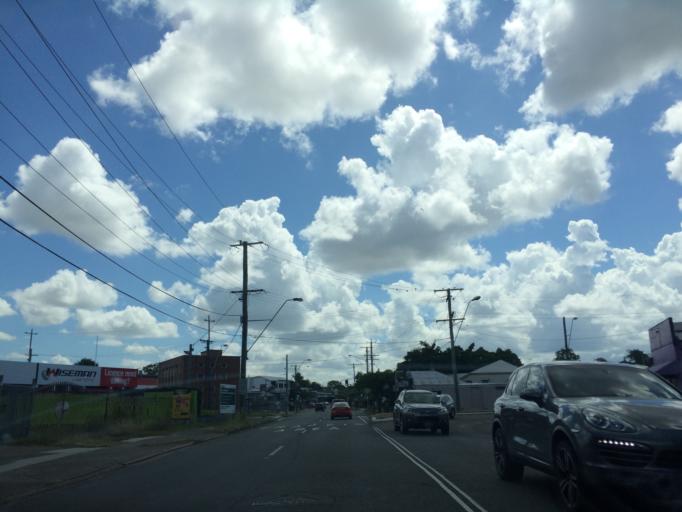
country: AU
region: Queensland
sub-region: Brisbane
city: Woolloongabba
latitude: -27.4877
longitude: 153.0508
